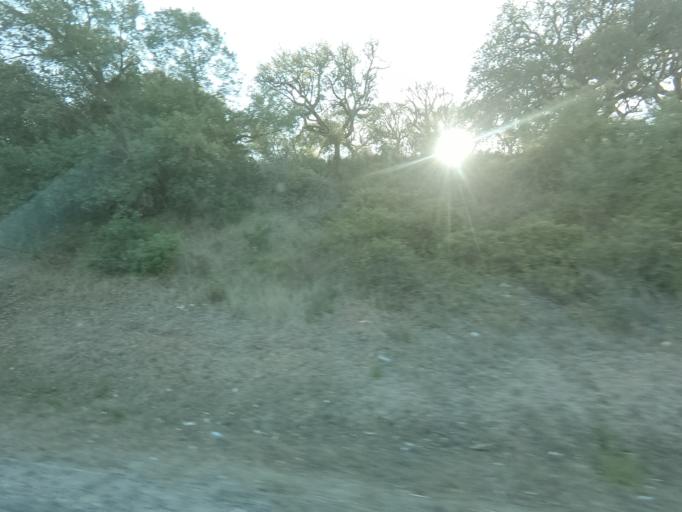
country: PT
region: Setubal
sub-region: Palmela
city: Quinta do Anjo
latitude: 38.5127
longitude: -8.9716
